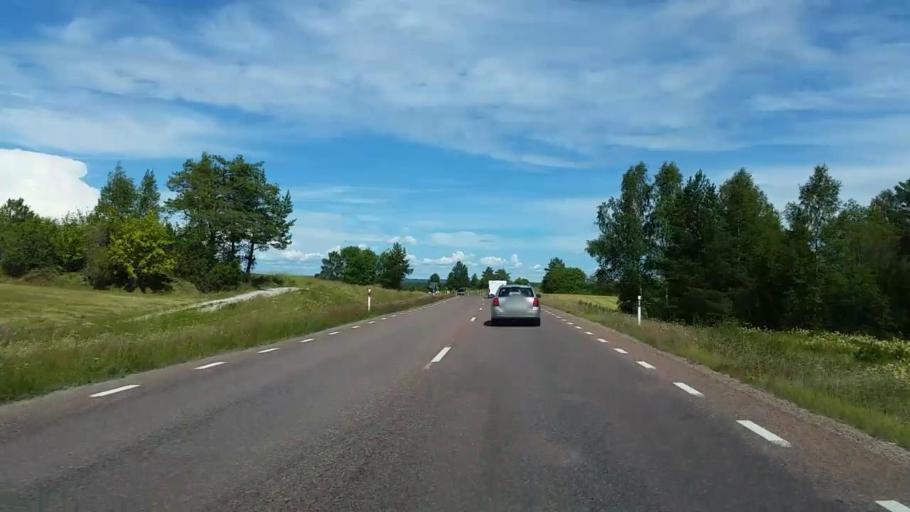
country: SE
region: Dalarna
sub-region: Rattviks Kommun
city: Raettvik
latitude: 60.9319
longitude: 15.2276
